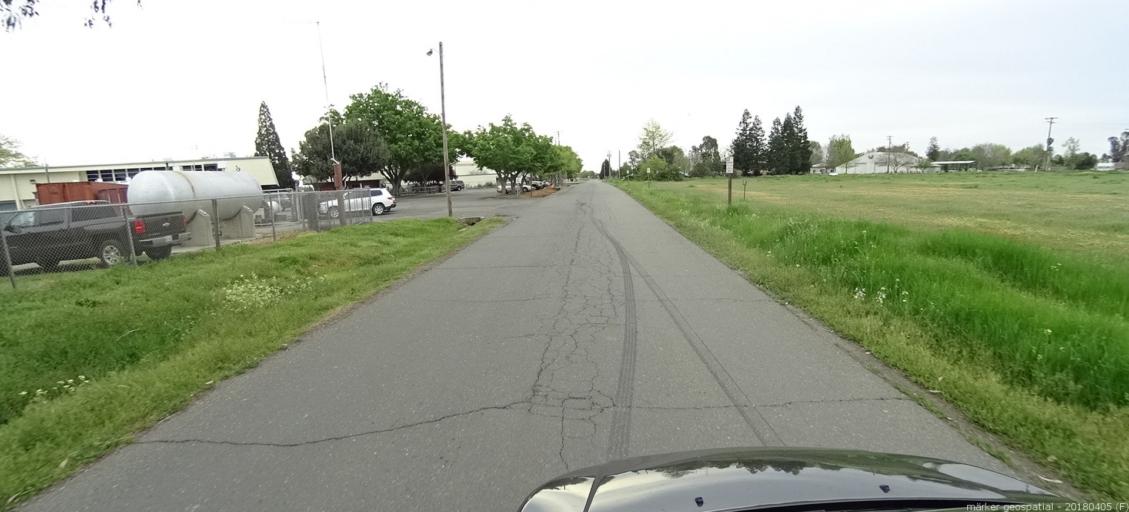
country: US
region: California
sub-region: Sacramento County
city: Herald
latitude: 38.2951
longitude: -121.2430
